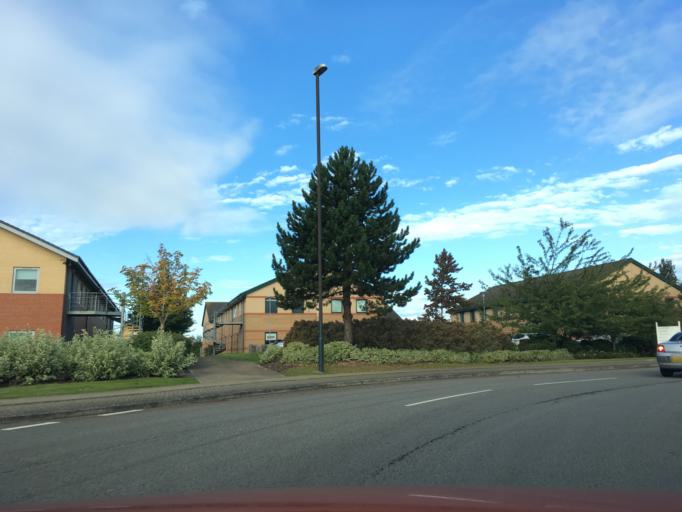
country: GB
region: England
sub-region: Gloucestershire
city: Barnwood
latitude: 51.8463
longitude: -2.1764
